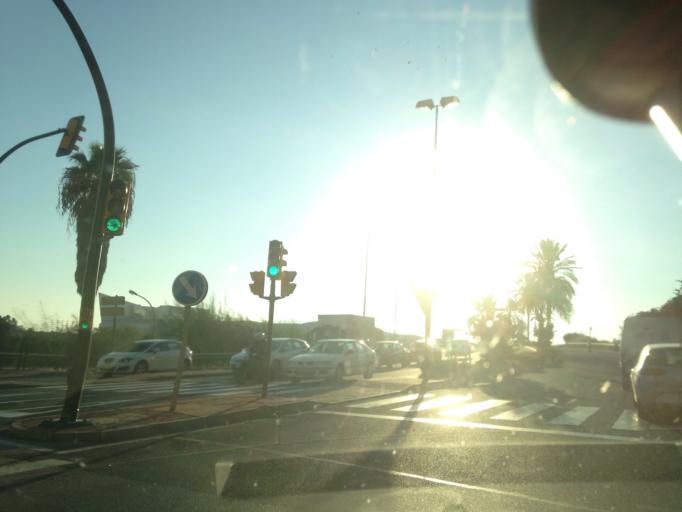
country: ES
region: Andalusia
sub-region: Provincia de Malaga
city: Malaga
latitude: 36.7096
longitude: -4.4556
